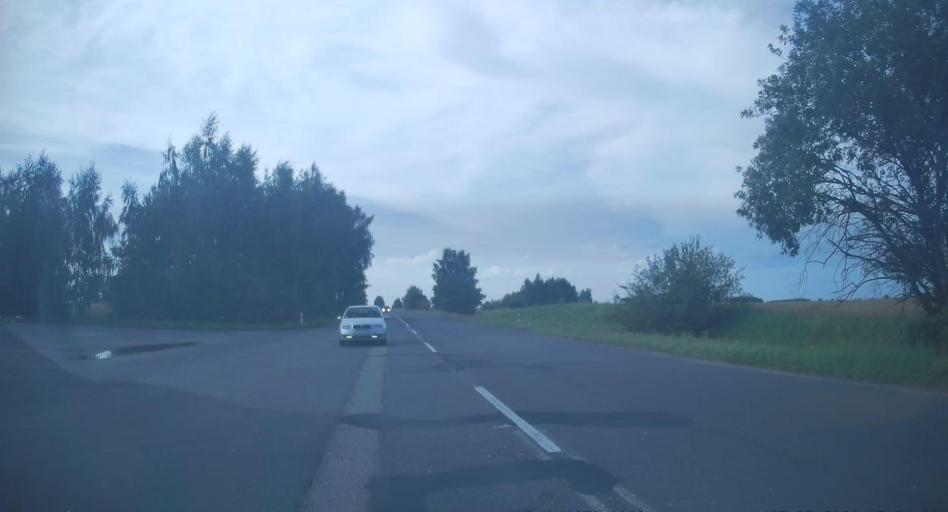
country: PL
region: Lodz Voivodeship
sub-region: Powiat tomaszowski
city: Rzeczyca
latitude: 51.6483
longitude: 20.2815
